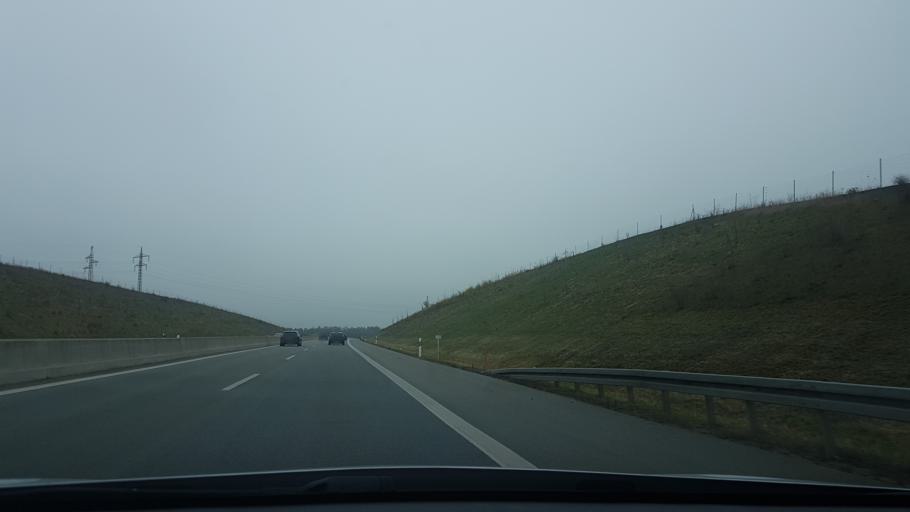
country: DE
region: Bavaria
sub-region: Lower Bavaria
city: Ergoldsbach
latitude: 48.6878
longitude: 12.1839
